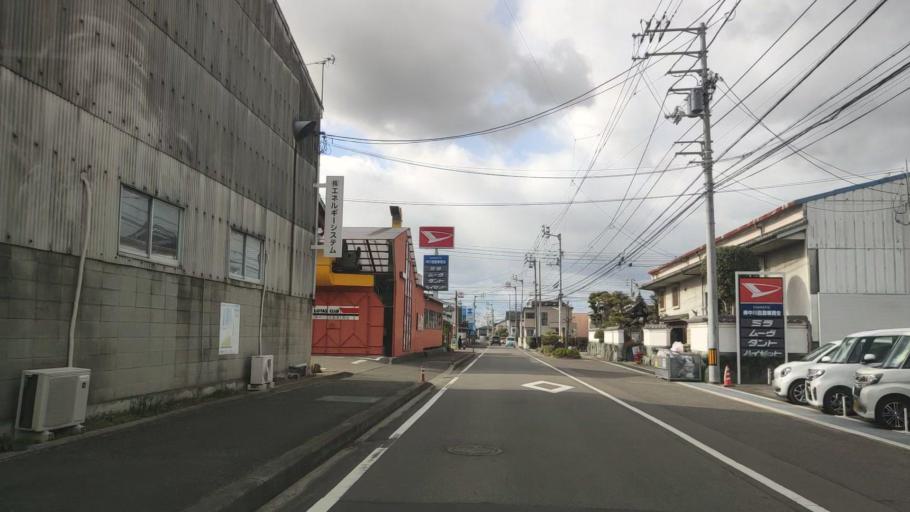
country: JP
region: Ehime
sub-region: Shikoku-chuo Shi
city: Matsuyama
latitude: 33.8098
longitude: 132.7925
